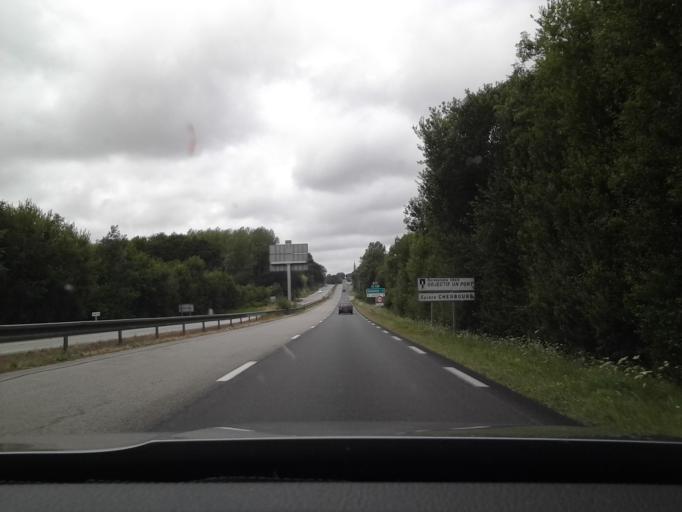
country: FR
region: Lower Normandy
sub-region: Departement de la Manche
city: Valognes
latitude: 49.5236
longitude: -1.5053
